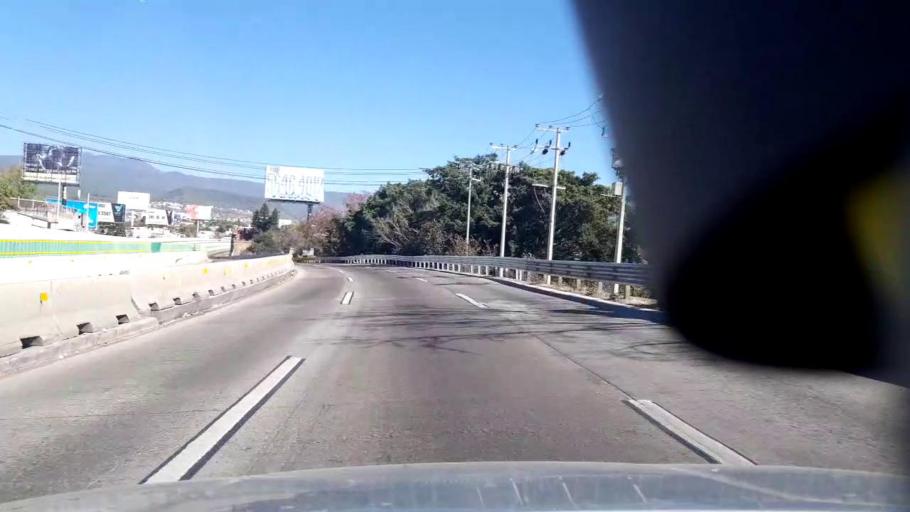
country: MX
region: Morelos
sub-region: Cuernavaca
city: Colonia los Cerritos
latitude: 18.9396
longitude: -99.1898
